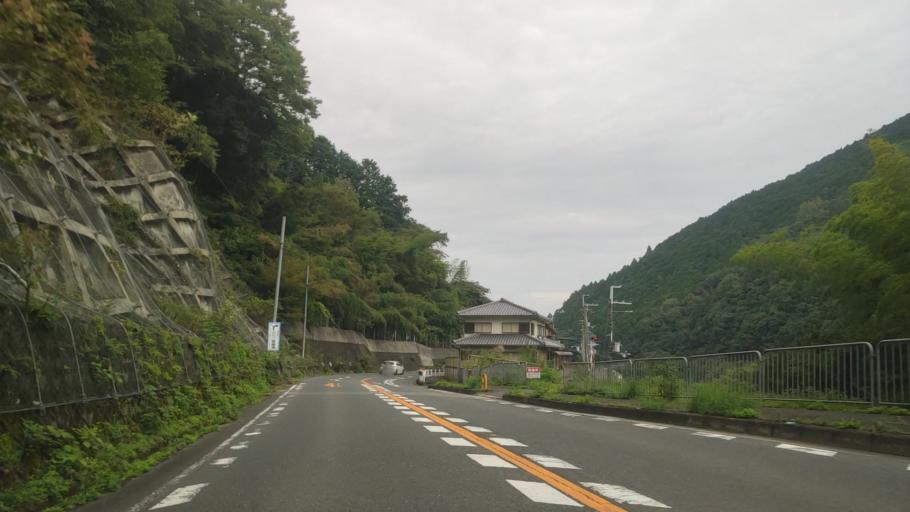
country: JP
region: Wakayama
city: Hashimoto
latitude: 34.3907
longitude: 135.5988
